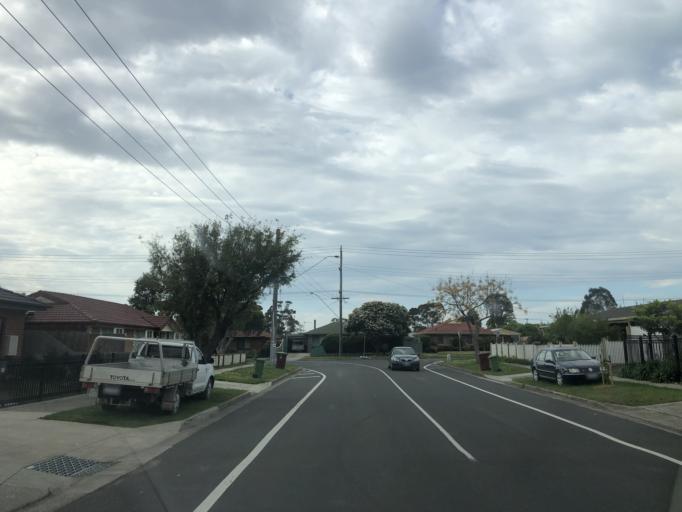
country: AU
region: Victoria
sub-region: Casey
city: Hampton Park
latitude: -38.0343
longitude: 145.2525
